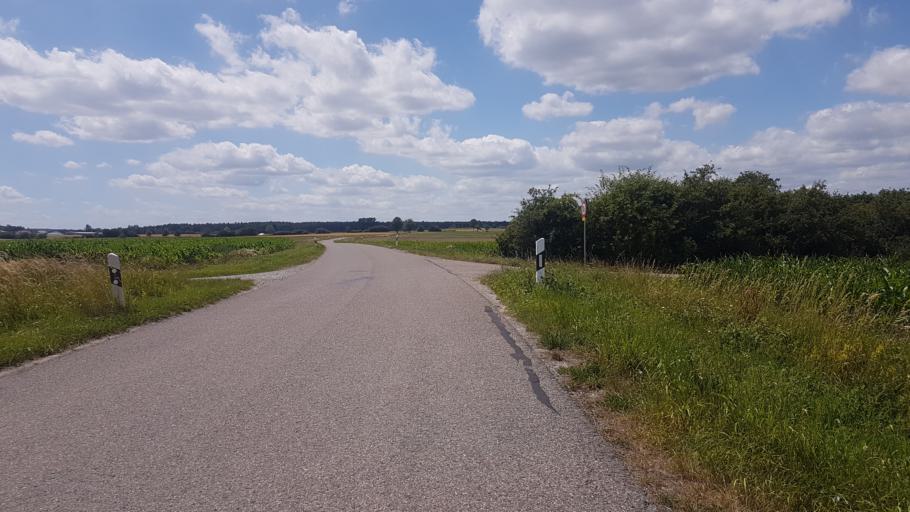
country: DE
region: Bavaria
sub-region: Regierungsbezirk Mittelfranken
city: Colmberg
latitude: 49.3326
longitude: 10.3537
